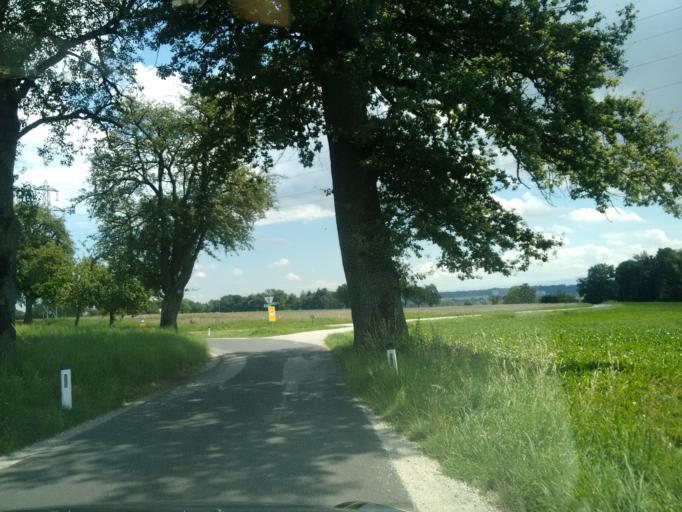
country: AT
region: Upper Austria
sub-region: Wels-Land
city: Gunskirchen
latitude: 48.1760
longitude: 13.9679
